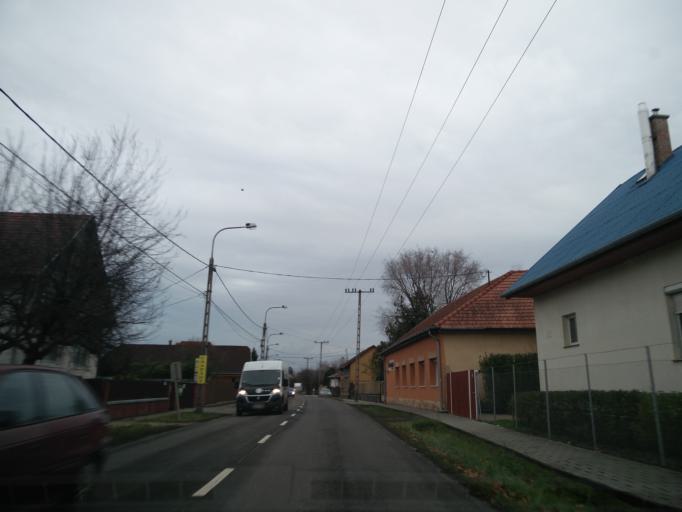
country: HU
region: Pest
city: Ullo
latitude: 47.3867
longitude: 19.3502
